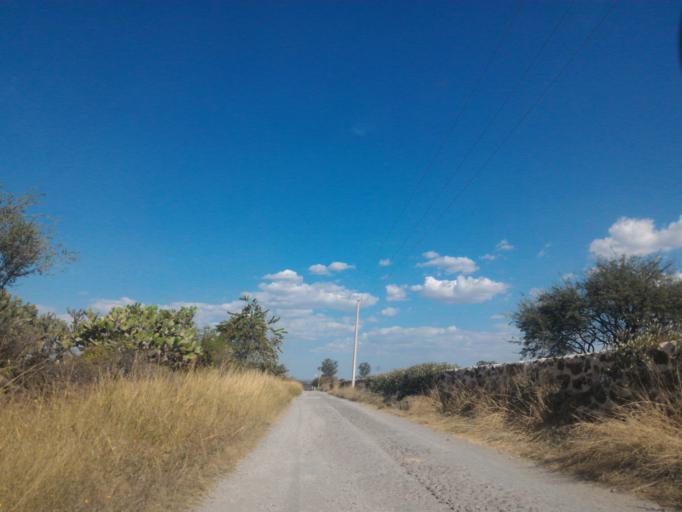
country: MX
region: Jalisco
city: San Diego de Alejandria
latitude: 20.8847
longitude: -101.9951
